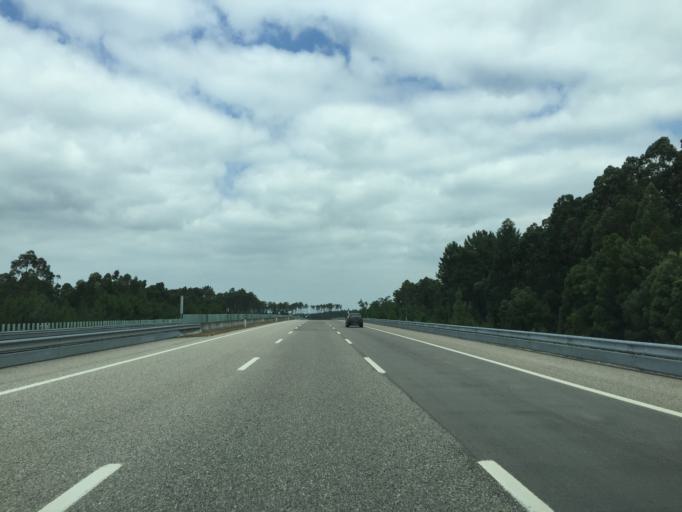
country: PT
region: Leiria
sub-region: Pombal
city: Lourical
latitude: 40.0141
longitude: -8.8074
